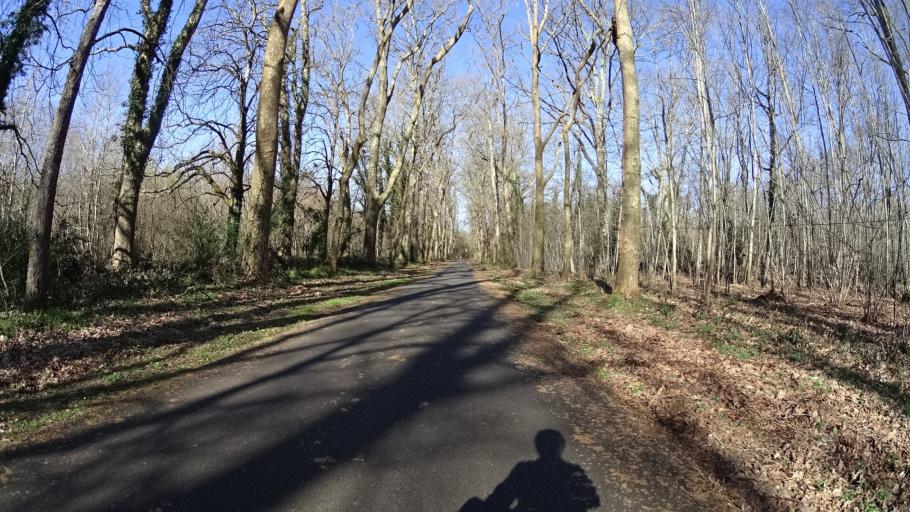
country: FR
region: Aquitaine
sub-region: Departement des Landes
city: Mees
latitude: 43.7473
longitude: -1.0962
